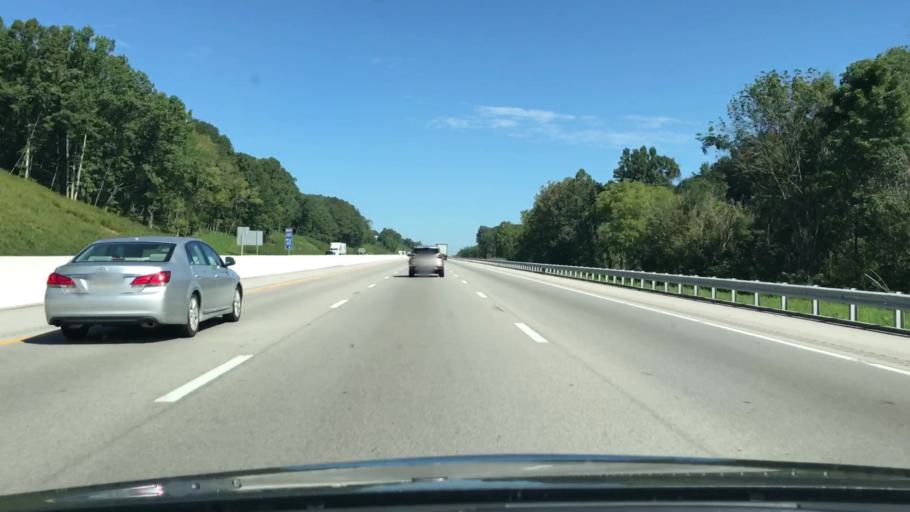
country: US
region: Kentucky
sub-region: Hart County
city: Munfordville
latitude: 37.3122
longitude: -85.9041
